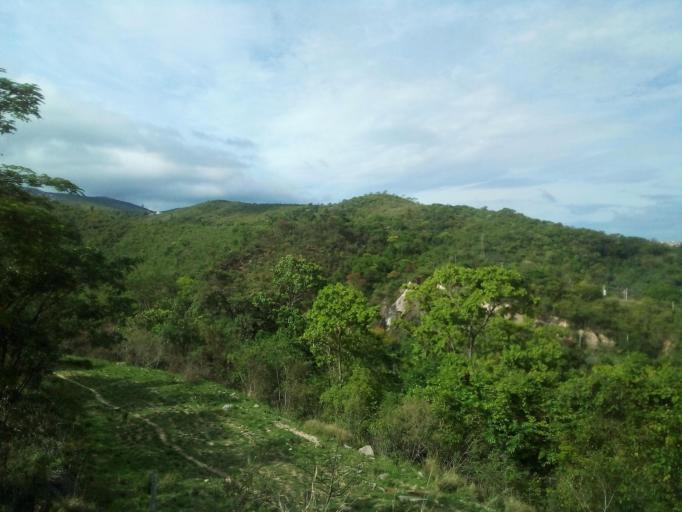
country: BR
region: Minas Gerais
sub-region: Belo Horizonte
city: Belo Horizonte
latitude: -19.8963
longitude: -43.8674
